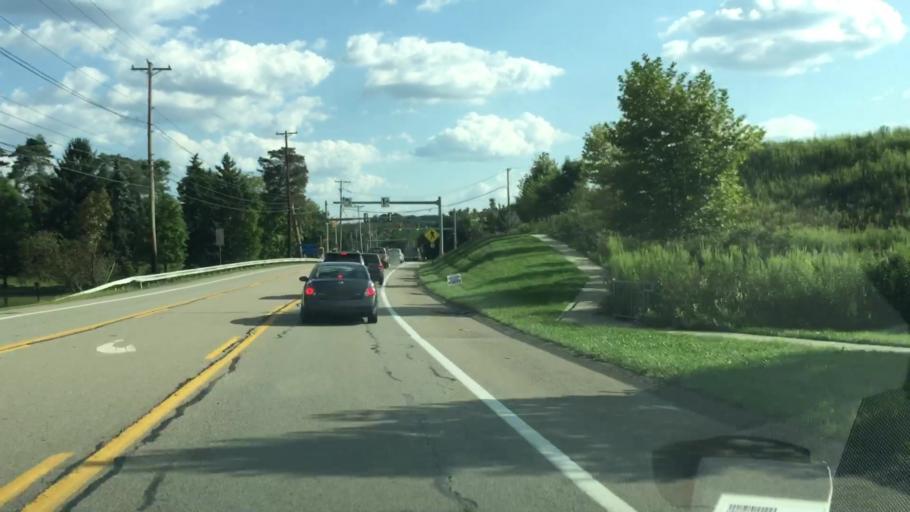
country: US
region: Pennsylvania
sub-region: Allegheny County
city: West View
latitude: 40.5706
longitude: -80.0163
